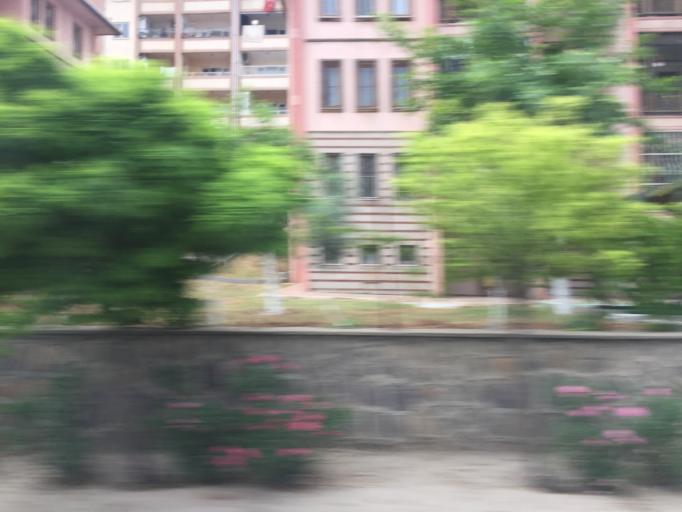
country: TR
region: Gaziantep
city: Gaziantep
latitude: 37.0526
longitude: 37.4204
